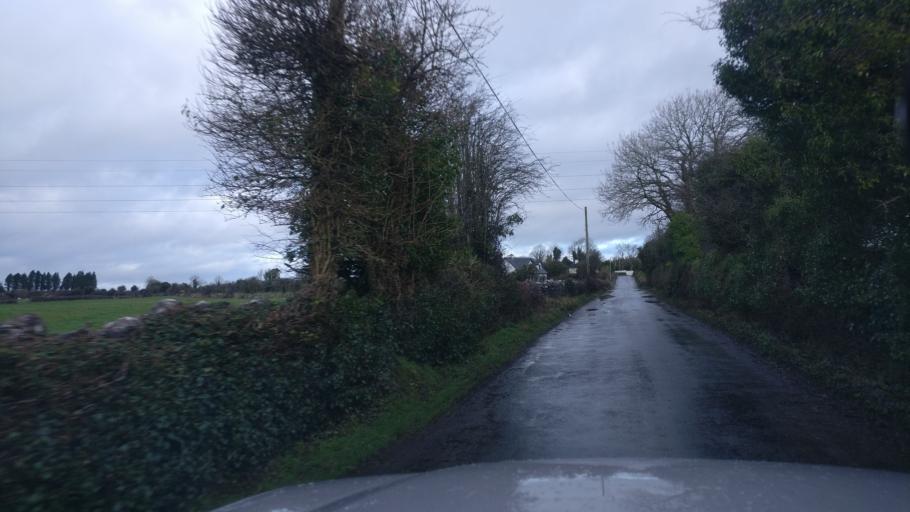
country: IE
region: Connaught
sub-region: County Galway
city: Loughrea
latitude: 53.2509
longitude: -8.6502
